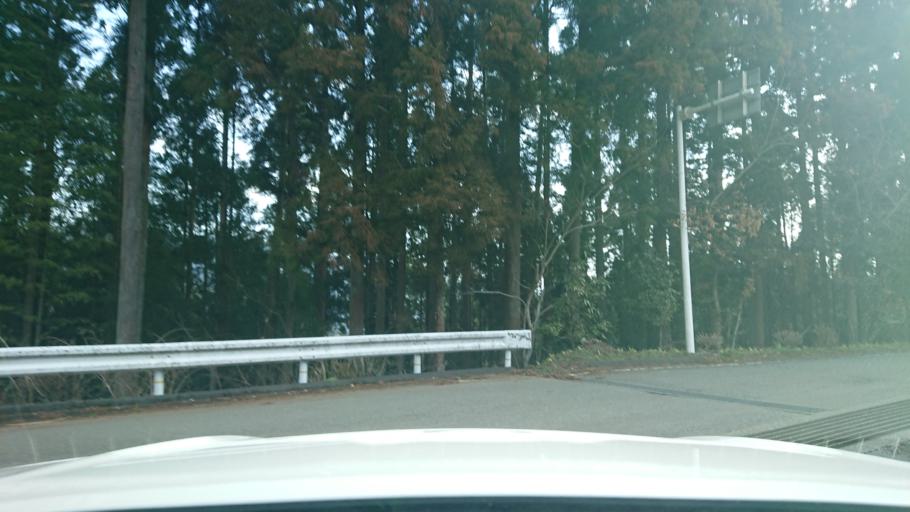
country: JP
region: Tokushima
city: Ishii
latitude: 33.9145
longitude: 134.4020
